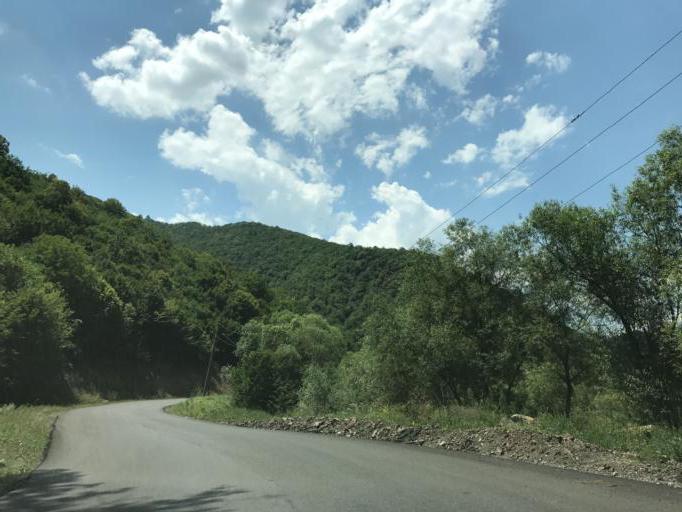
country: AZ
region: Kalbacar Rayonu
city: Kerbakhiar
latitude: 40.2282
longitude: 46.1664
